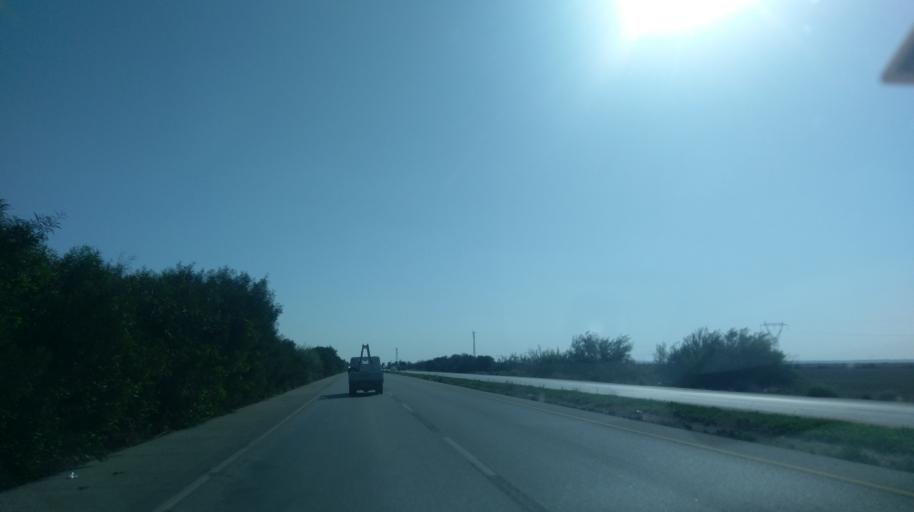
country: CY
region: Ammochostos
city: Acheritou
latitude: 35.1634
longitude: 33.8298
